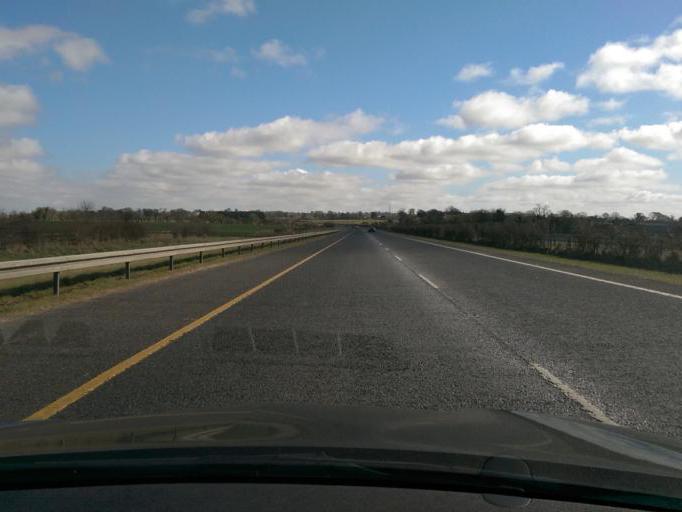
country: IE
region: Leinster
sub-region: An Mhi
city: Enfield
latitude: 53.4047
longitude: -6.8061
